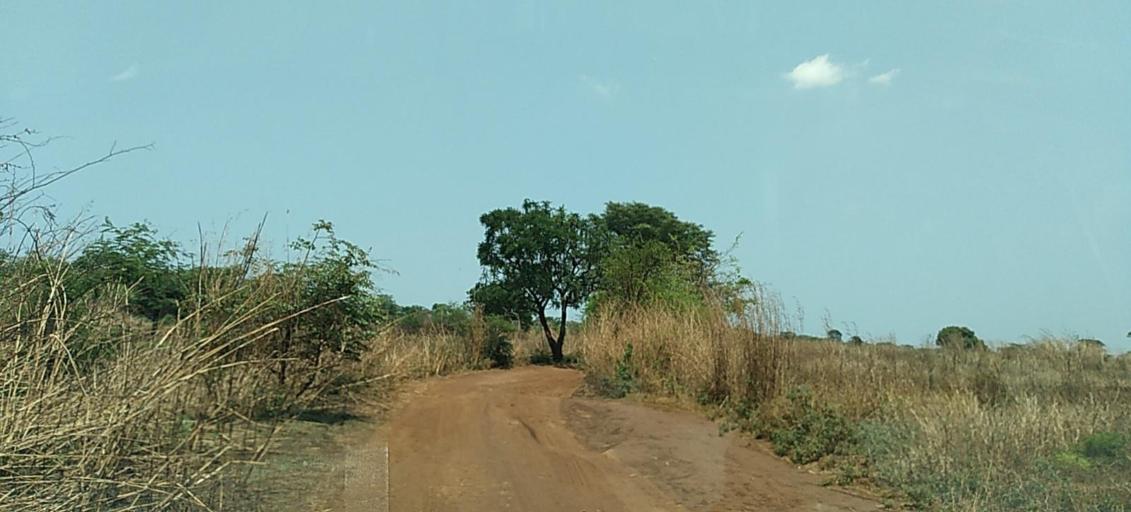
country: ZM
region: Copperbelt
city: Mpongwe
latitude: -13.8382
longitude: 27.8430
